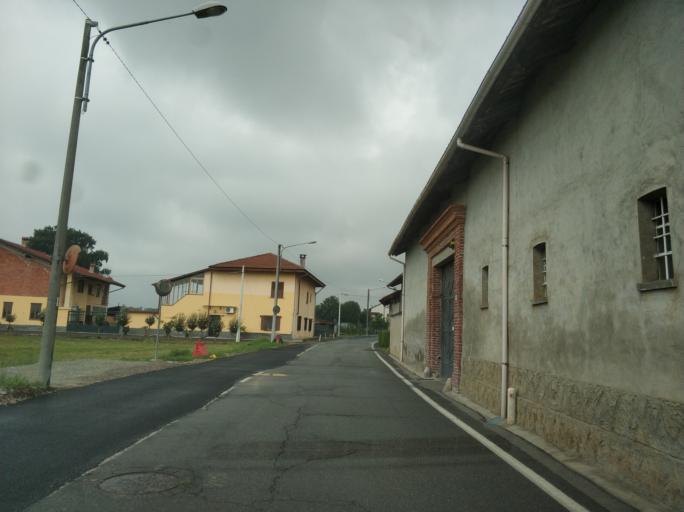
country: IT
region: Piedmont
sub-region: Provincia di Torino
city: San Francesco al Campo
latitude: 45.2153
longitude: 7.6840
